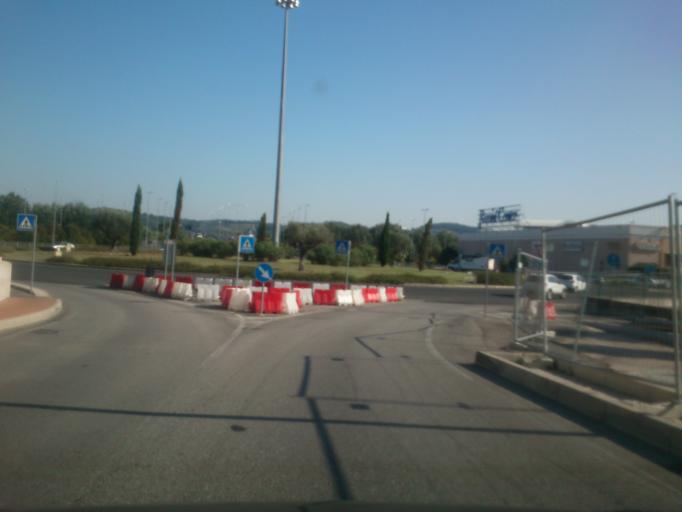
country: IT
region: The Marches
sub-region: Provincia di Pesaro e Urbino
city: Pesaro
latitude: 43.9072
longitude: 12.8694
